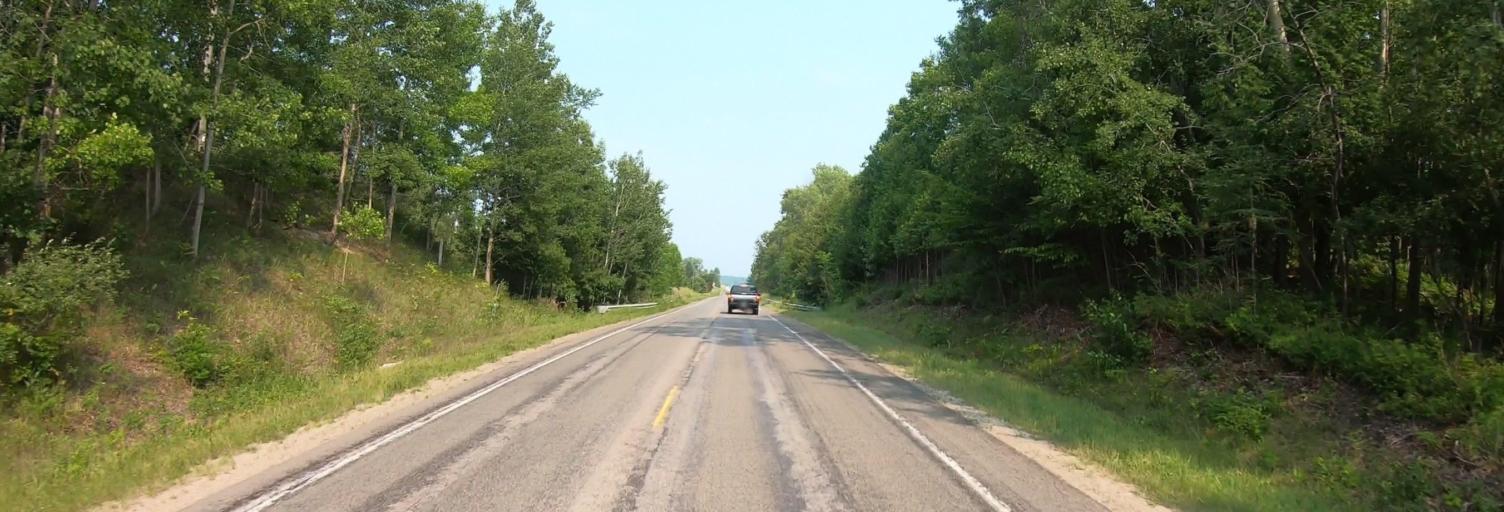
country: US
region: Michigan
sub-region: Charlevoix County
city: Charlevoix
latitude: 45.1842
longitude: -85.2710
